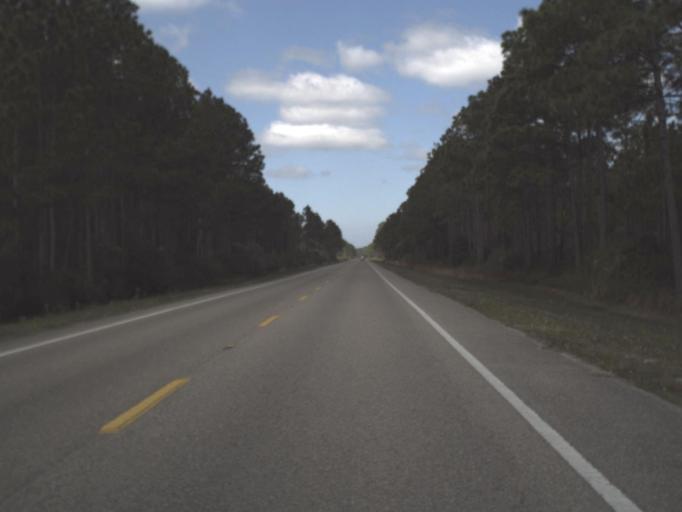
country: US
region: Florida
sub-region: Franklin County
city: Apalachicola
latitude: 29.7277
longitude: -85.1307
